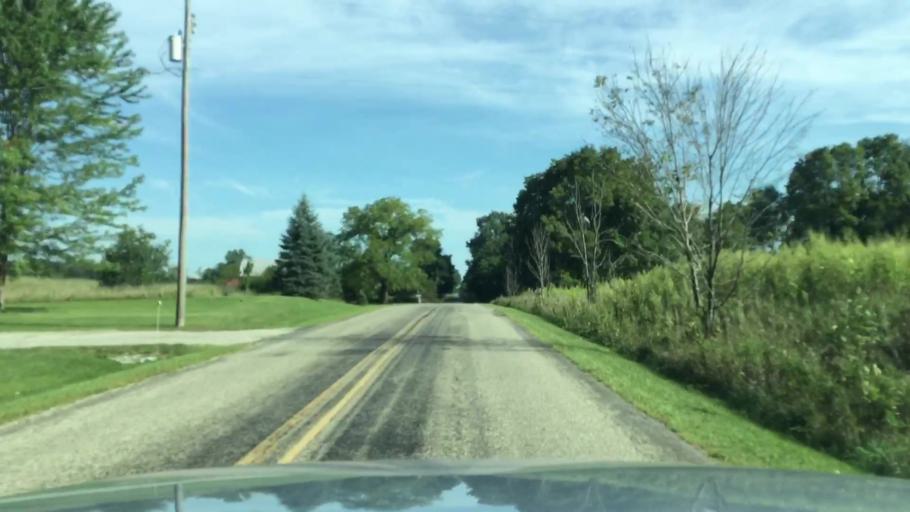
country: US
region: Michigan
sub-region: Lenawee County
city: Hudson
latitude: 41.8899
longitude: -84.4203
